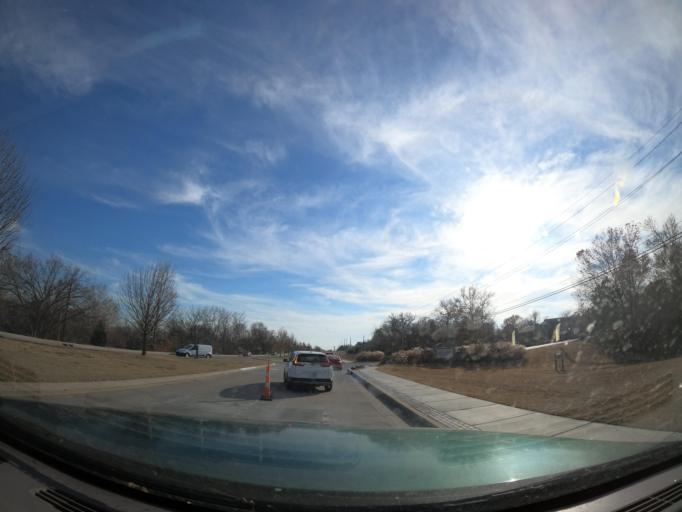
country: US
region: Oklahoma
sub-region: Tulsa County
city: Jenks
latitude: 36.0413
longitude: -95.8863
